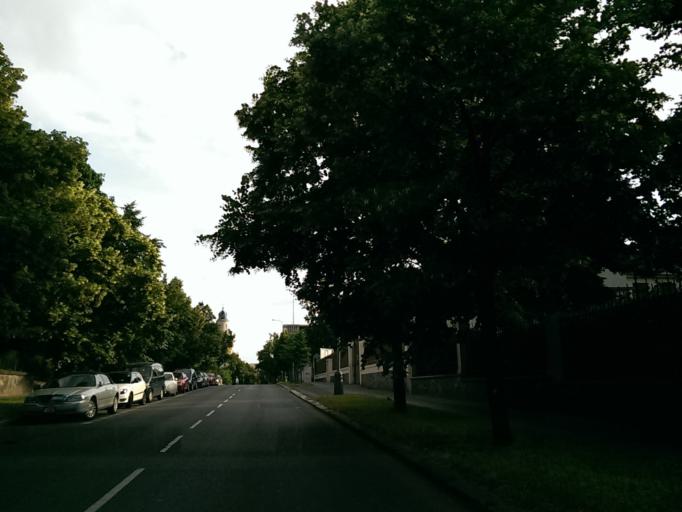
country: CZ
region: Praha
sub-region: Praha 8
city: Karlin
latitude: 50.0811
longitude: 14.4386
